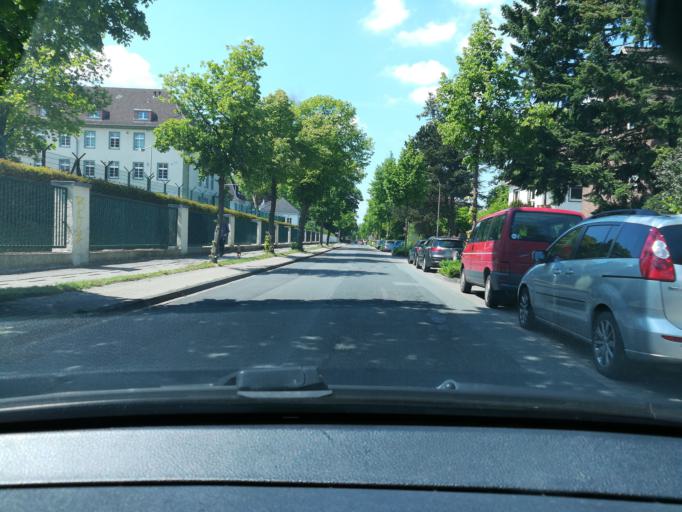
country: DE
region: North Rhine-Westphalia
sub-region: Regierungsbezirk Detmold
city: Herford
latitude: 52.1155
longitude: 8.6935
